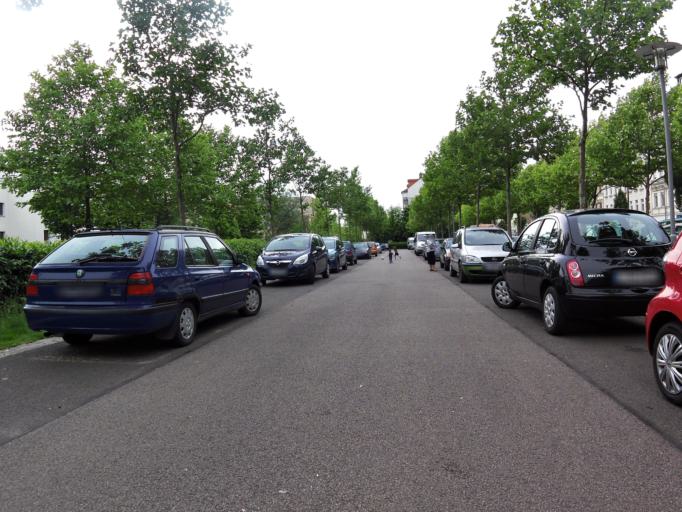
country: DE
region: Saxony
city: Leipzig
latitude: 51.3455
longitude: 12.4031
